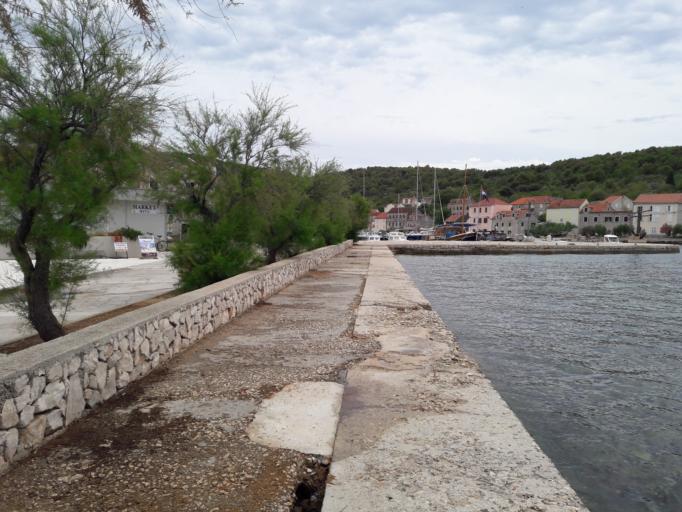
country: HR
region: Sibensko-Kniniska
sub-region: Grad Sibenik
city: Sibenik
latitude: 43.6990
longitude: 15.8344
